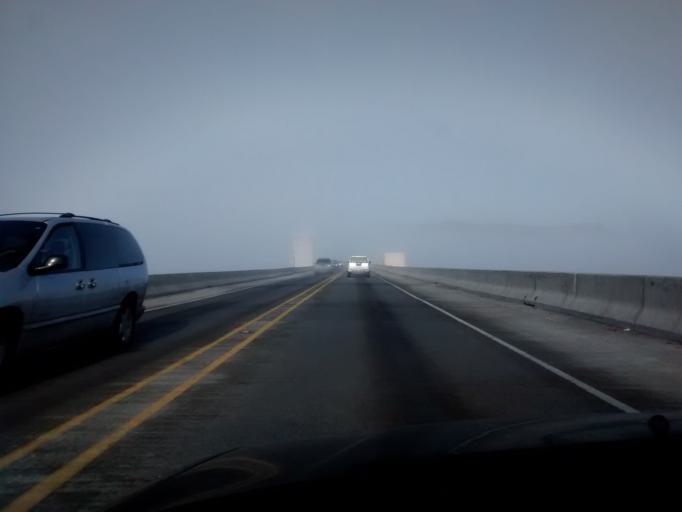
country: US
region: Washington
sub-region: Kitsap County
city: Lofall
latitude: 47.8586
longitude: -122.6222
